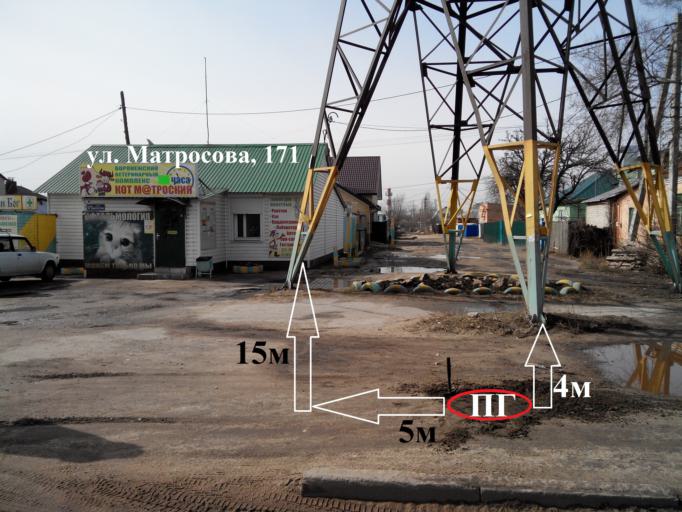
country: RU
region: Voronezj
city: Voronezh
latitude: 51.6425
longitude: 39.1551
